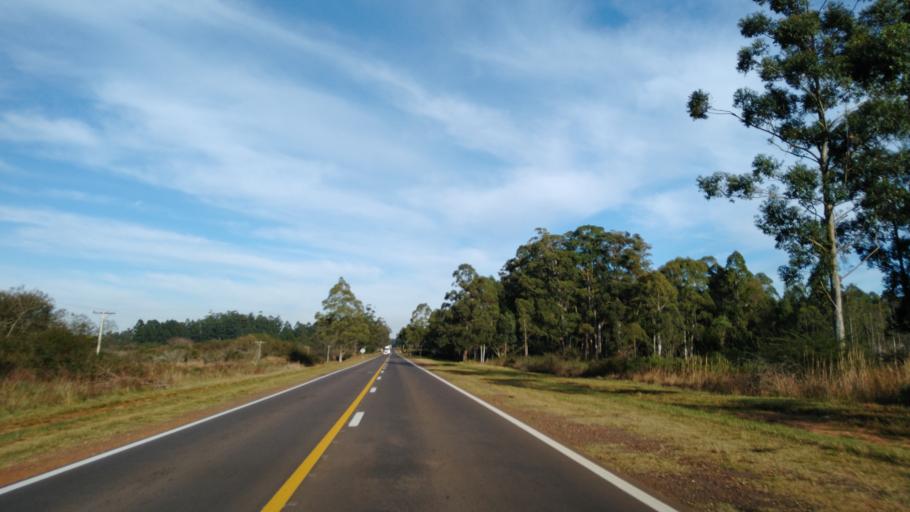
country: AR
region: Corrientes
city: Yapeyu
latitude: -29.4250
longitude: -56.8611
